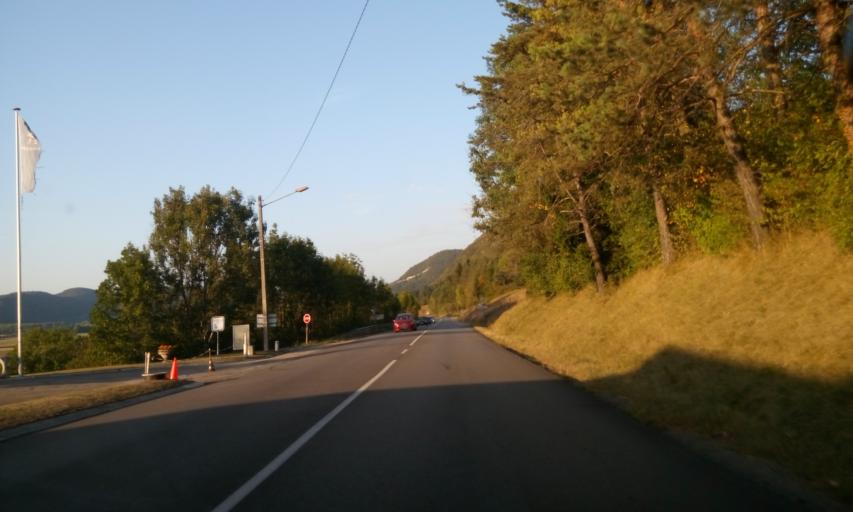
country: FR
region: Rhone-Alpes
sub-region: Departement de l'Ain
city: Saint-Martin-du-Frene
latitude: 46.1439
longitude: 5.5559
